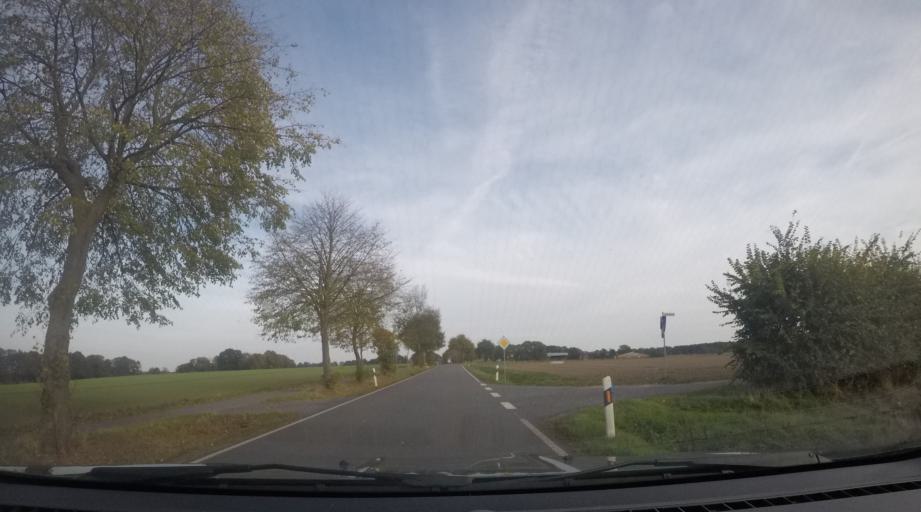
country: DE
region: North Rhine-Westphalia
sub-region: Regierungsbezirk Dusseldorf
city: Bocholt
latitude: 51.8154
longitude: 6.6542
